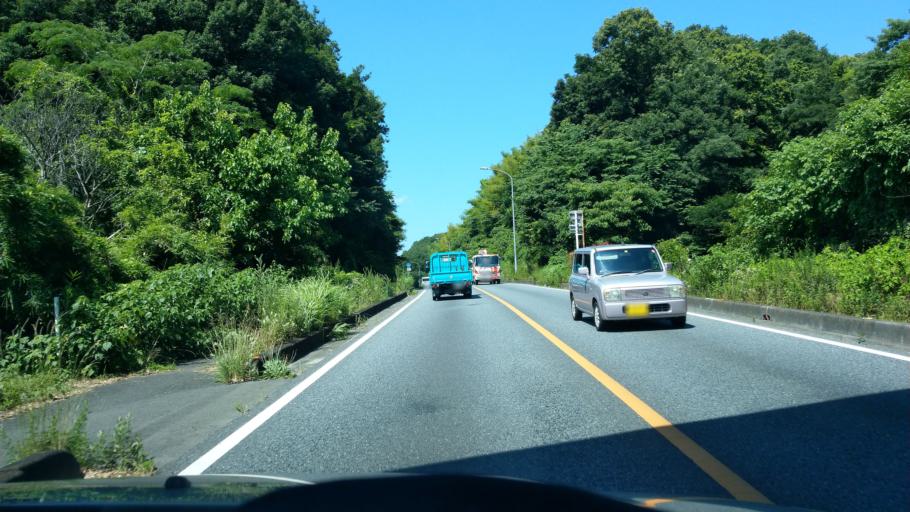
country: JP
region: Saitama
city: Ogawa
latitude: 36.0703
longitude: 139.2716
